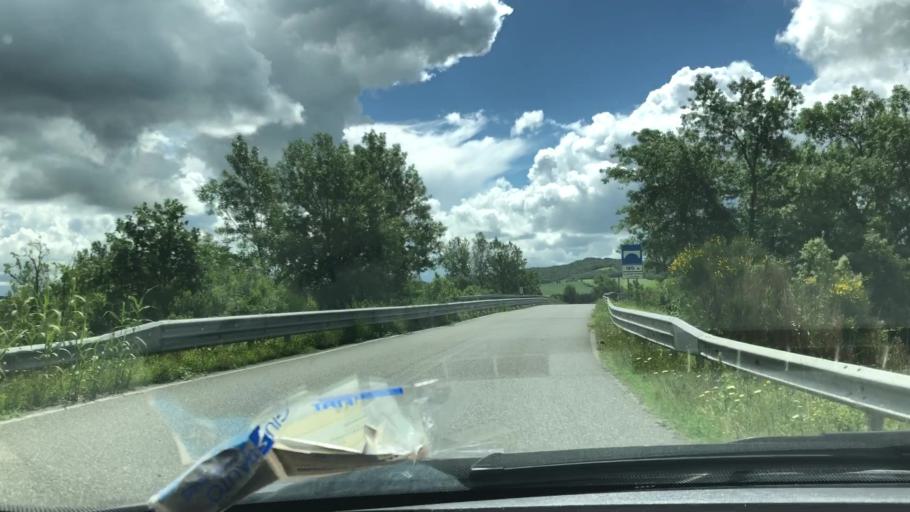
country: IT
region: Tuscany
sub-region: Province of Pisa
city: Saline
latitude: 43.3552
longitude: 10.7846
